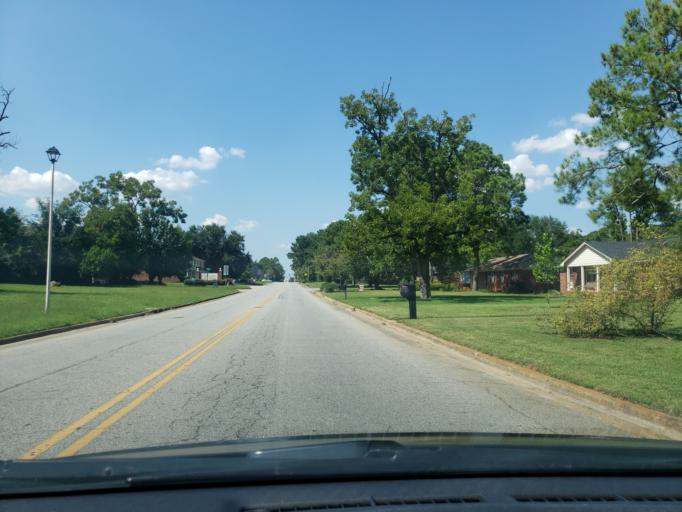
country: US
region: Georgia
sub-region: Dougherty County
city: Albany
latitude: 31.6085
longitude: -84.2042
